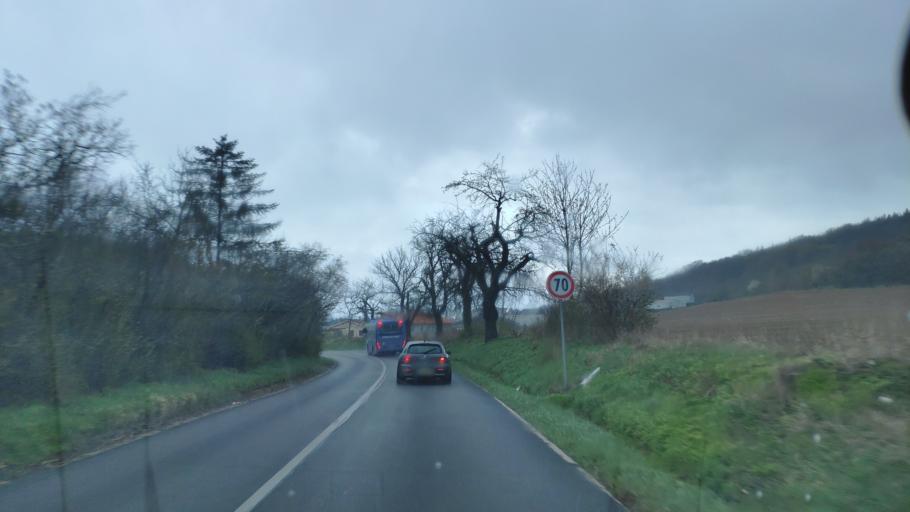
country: SK
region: Trenciansky
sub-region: Okres Nove Mesto nad Vahom
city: Nove Mesto nad Vahom
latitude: 48.7708
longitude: 17.8169
